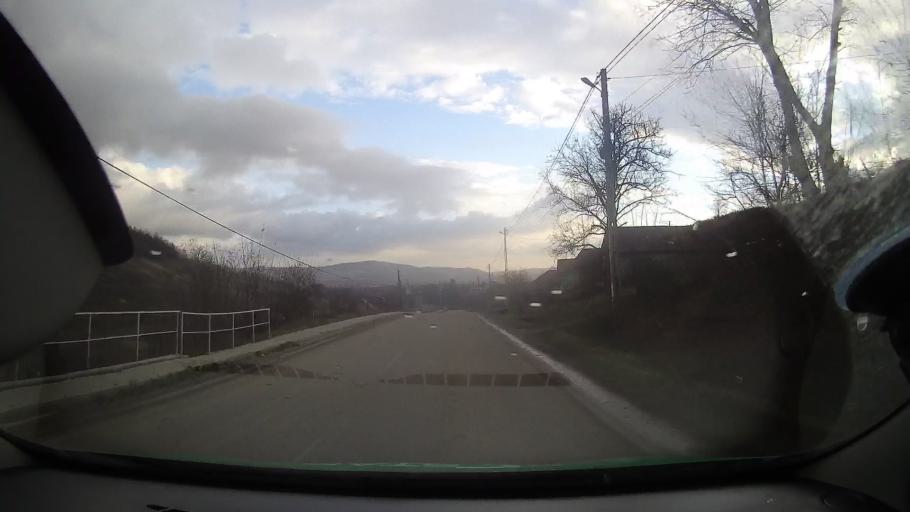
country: RO
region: Alba
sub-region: Comuna Lunca Muresului
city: Lunca Muresului
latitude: 46.4319
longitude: 23.9087
